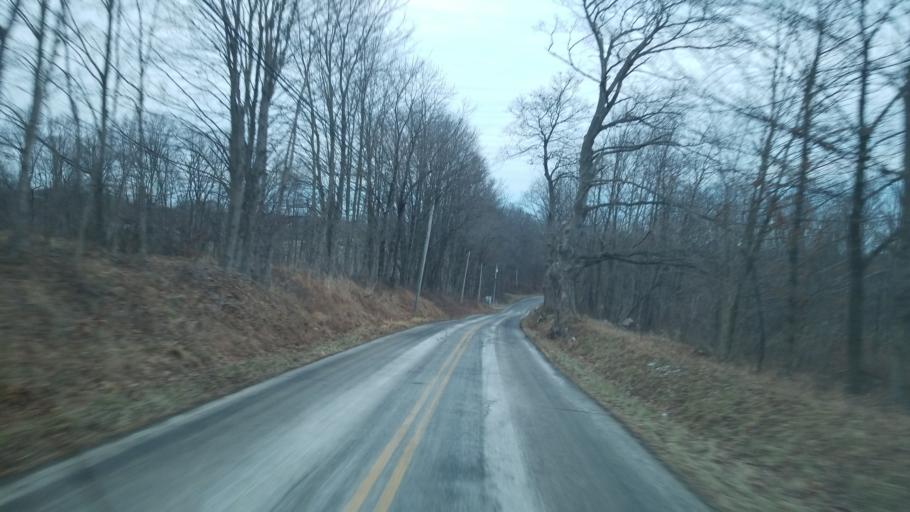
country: US
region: Ohio
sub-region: Holmes County
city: Millersburg
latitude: 40.4896
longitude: -81.8749
